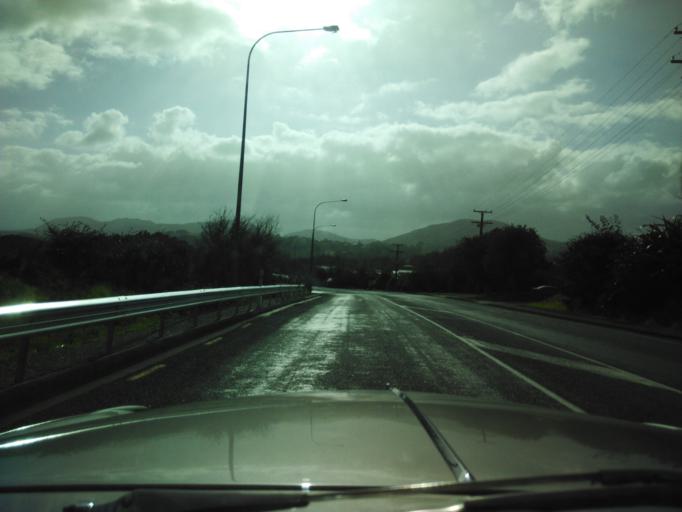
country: NZ
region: Auckland
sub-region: Auckland
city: Wellsford
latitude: -36.1681
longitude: 174.4460
